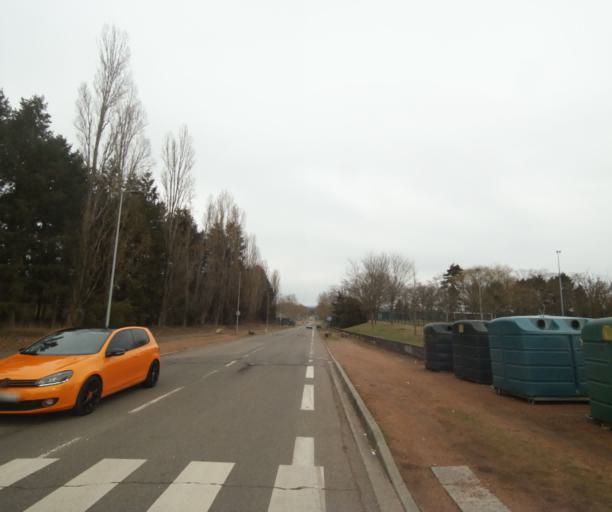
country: FR
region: Rhone-Alpes
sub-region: Departement de la Loire
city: Mably
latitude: 46.0670
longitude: 4.0791
